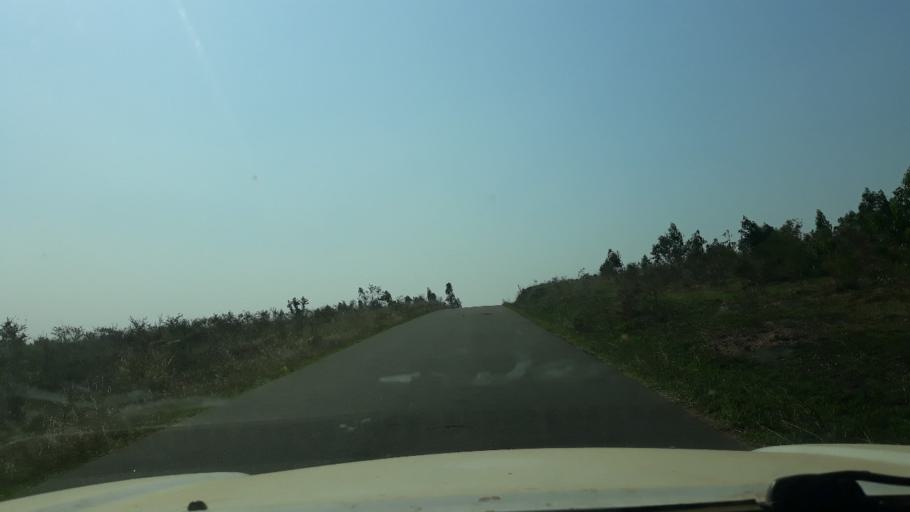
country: BI
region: Cibitoke
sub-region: Commune of Buganda
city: Buganda
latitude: -3.0105
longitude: 29.1023
